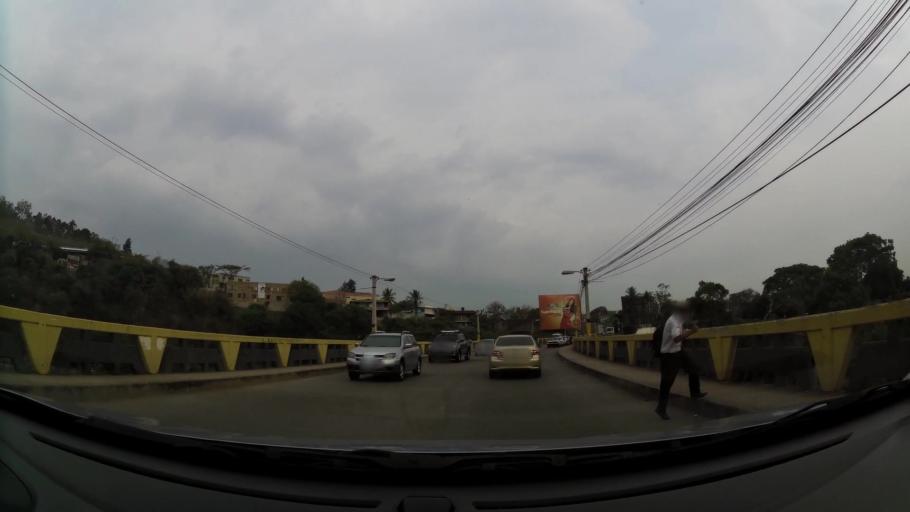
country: HN
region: Francisco Morazan
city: Tegucigalpa
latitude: 14.0892
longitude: -87.2049
